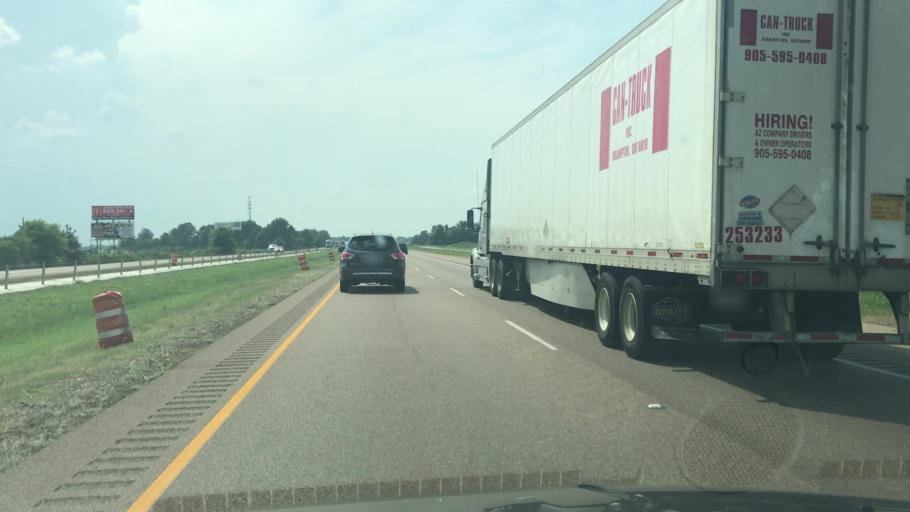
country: US
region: Arkansas
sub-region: Crittenden County
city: West Memphis
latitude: 35.1492
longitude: -90.3490
